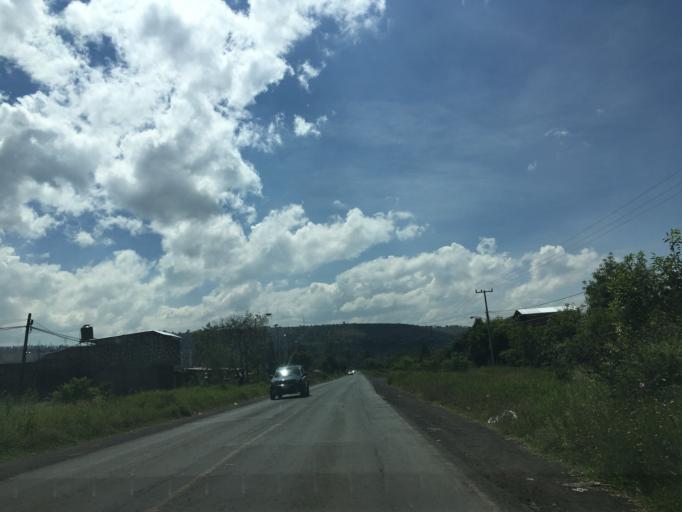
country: MX
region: Michoacan
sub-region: Morelia
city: La Mintzita (Piedra Dura)
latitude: 19.6549
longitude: -101.2796
